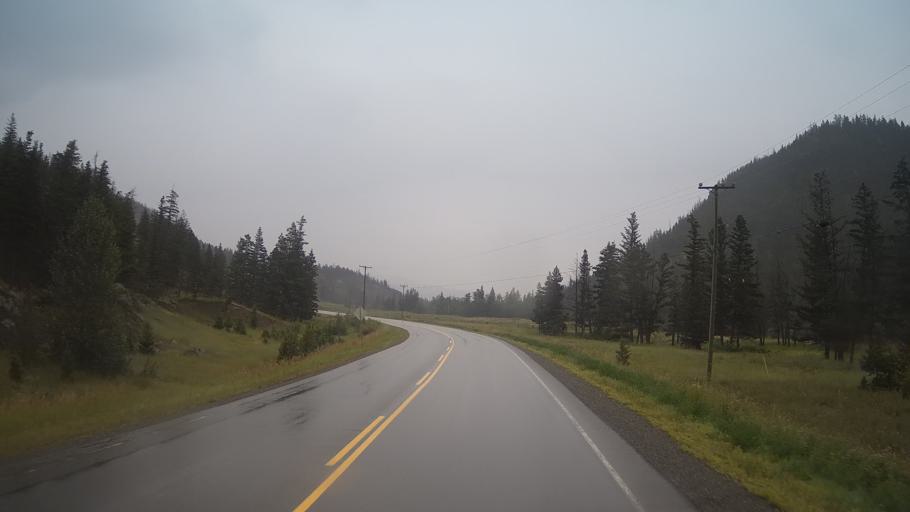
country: CA
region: British Columbia
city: Hanceville
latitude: 52.0859
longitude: -123.3615
